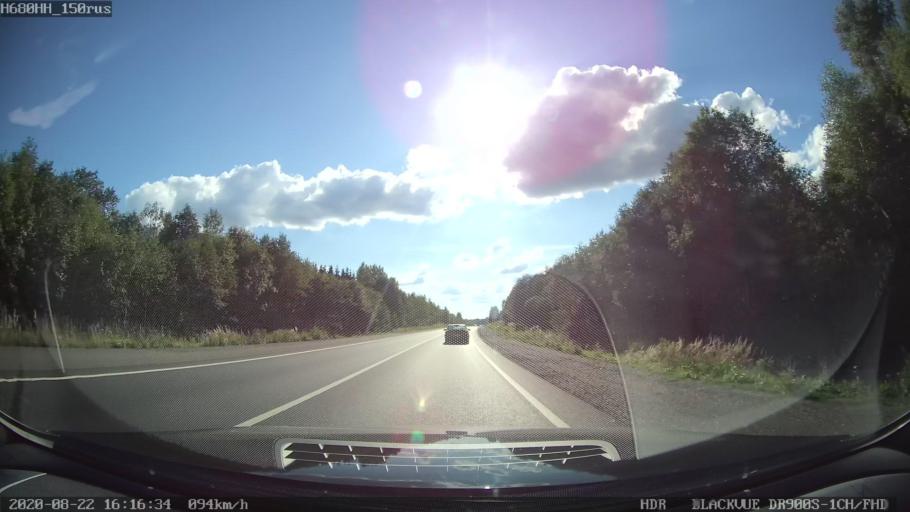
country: RU
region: Tverskaya
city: Rameshki
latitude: 57.4326
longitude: 36.1770
